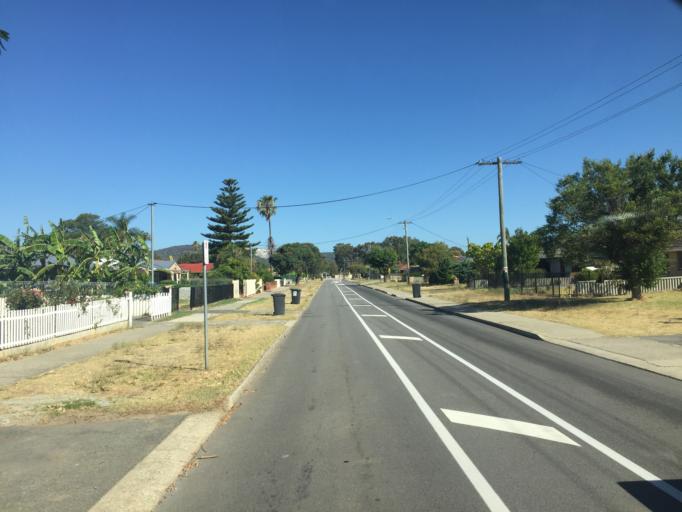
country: AU
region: Western Australia
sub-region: Gosnells
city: Maddington
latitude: -32.0492
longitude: 115.9974
